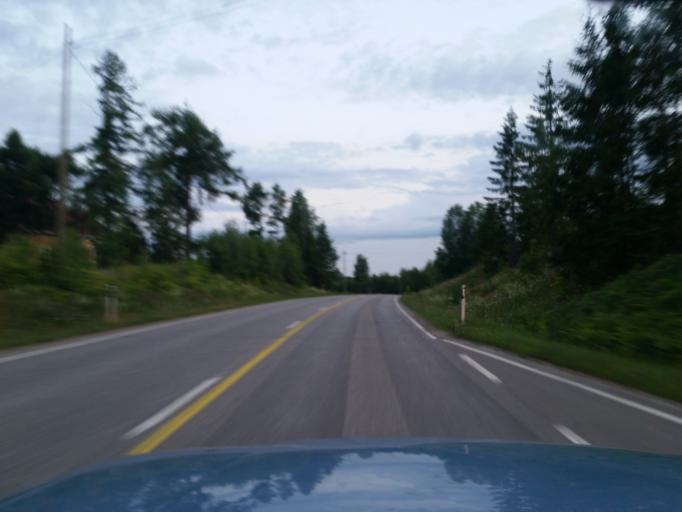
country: FI
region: Southern Savonia
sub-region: Savonlinna
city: Sulkava
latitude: 61.8180
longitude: 28.4367
